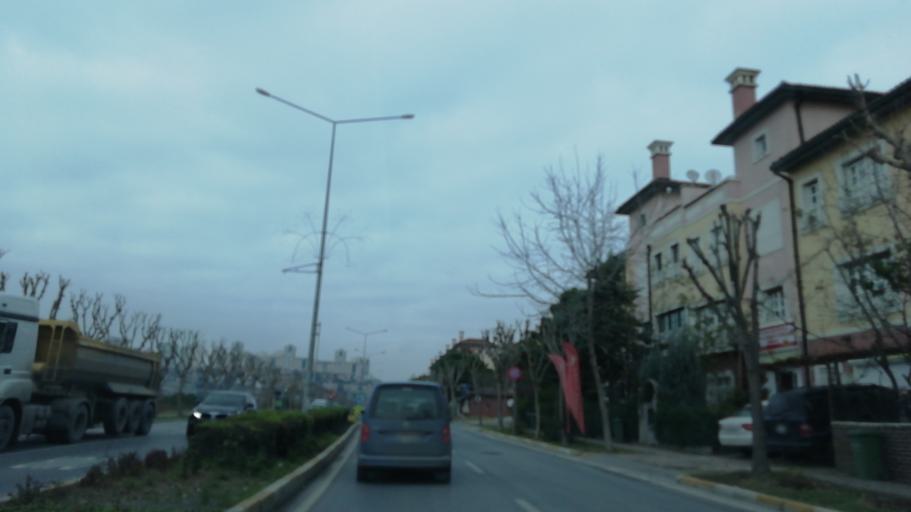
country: TR
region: Istanbul
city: Esenyurt
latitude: 41.0653
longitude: 28.6987
